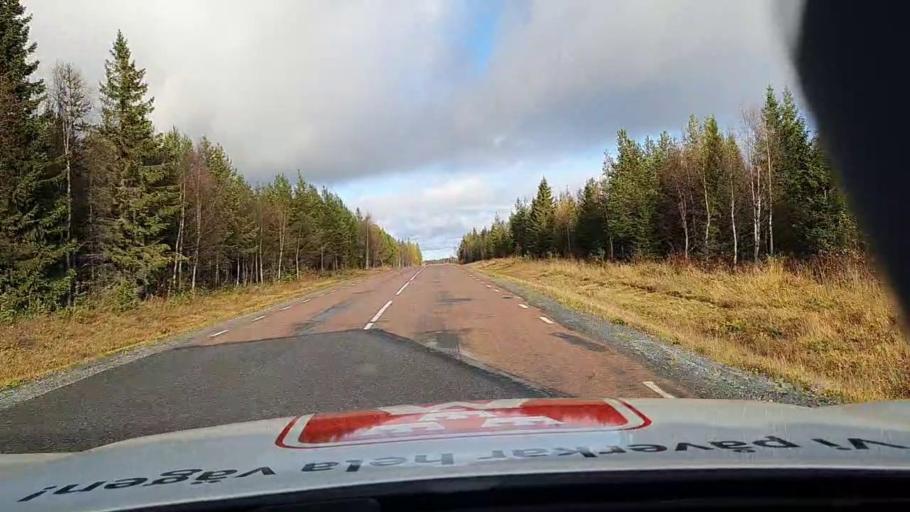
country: SE
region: Jaemtland
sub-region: Krokoms Kommun
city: Valla
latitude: 63.1291
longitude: 13.9337
